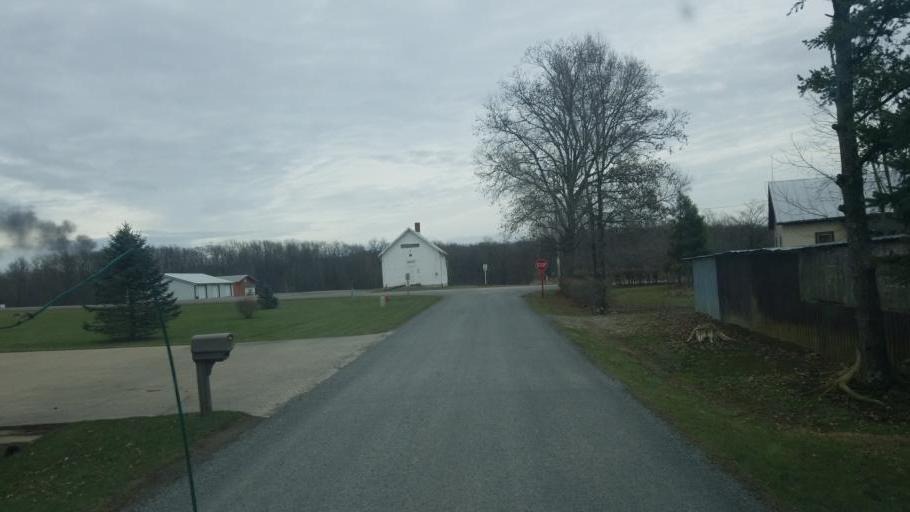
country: US
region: Ohio
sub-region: Delaware County
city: Ashley
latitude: 40.3920
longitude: -82.8770
